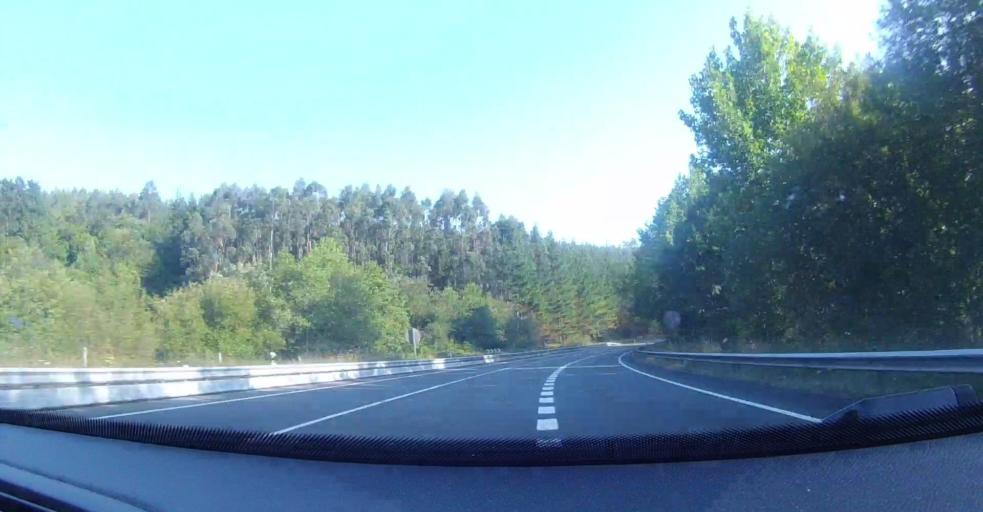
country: ES
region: Cantabria
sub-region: Provincia de Cantabria
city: Limpias
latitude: 43.3642
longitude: -3.4132
